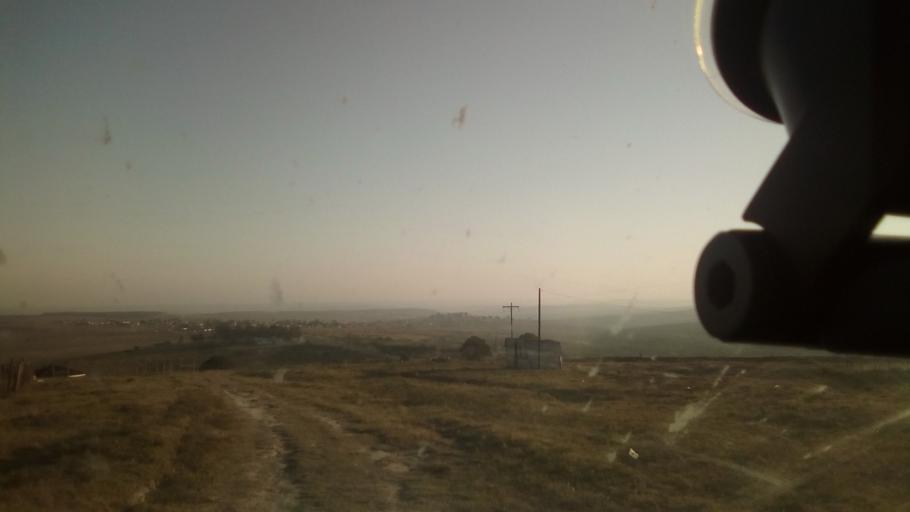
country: ZA
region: Eastern Cape
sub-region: Buffalo City Metropolitan Municipality
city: Bhisho
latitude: -32.9731
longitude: 27.2915
